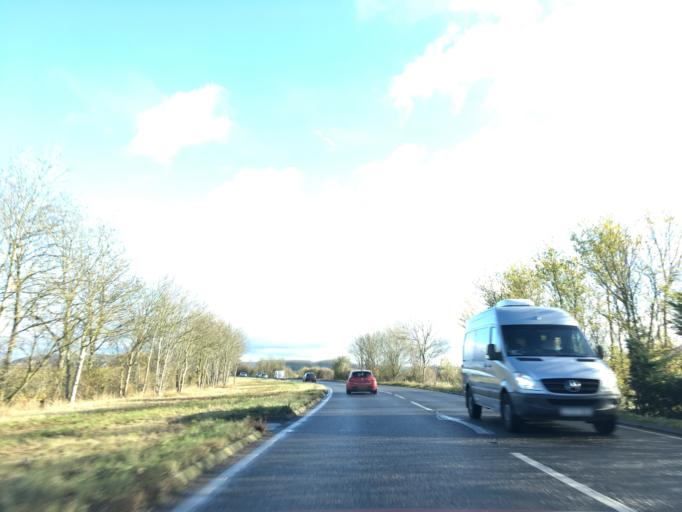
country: GB
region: England
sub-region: Gloucestershire
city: Gotherington
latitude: 52.0012
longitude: -2.0736
